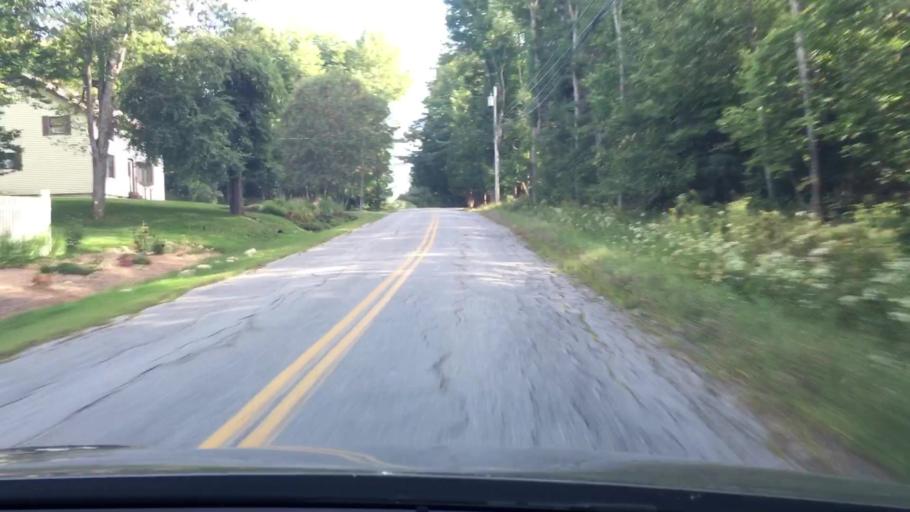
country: US
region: Maine
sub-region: Hancock County
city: Bucksport
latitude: 44.5483
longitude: -68.7974
